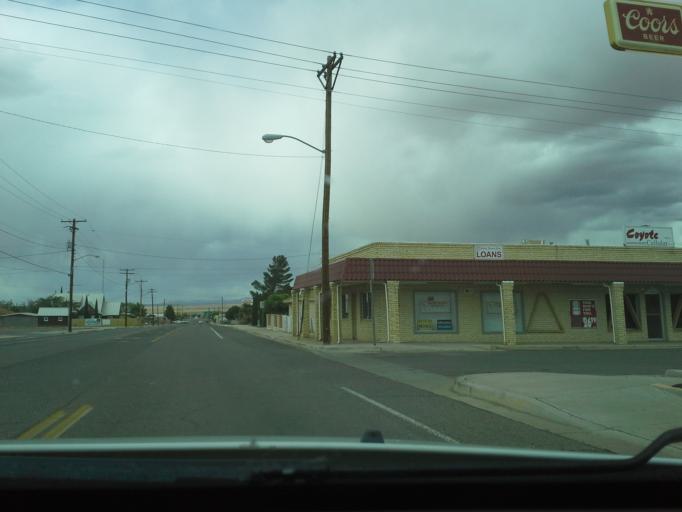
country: US
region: New Mexico
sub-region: Hidalgo County
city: Lordsburg
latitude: 32.3447
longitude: -108.7107
